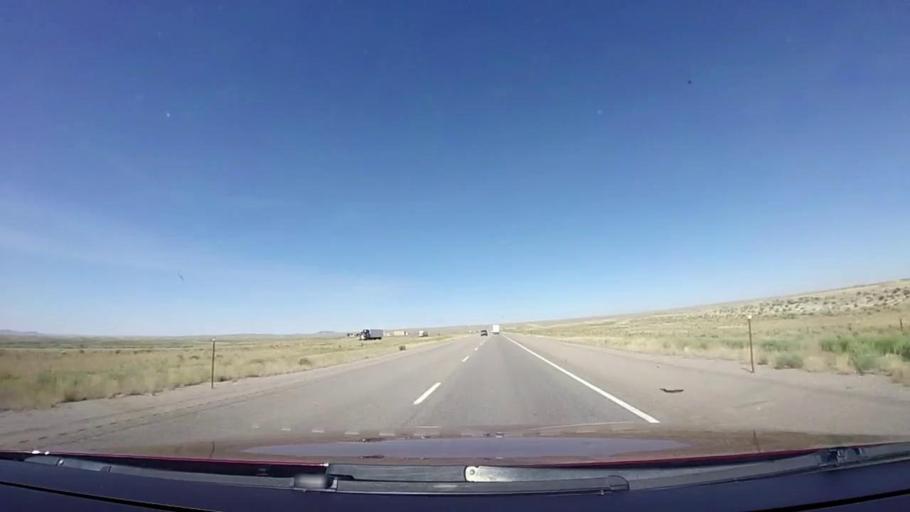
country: US
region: Wyoming
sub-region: Sweetwater County
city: Rock Springs
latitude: 41.6396
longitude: -108.4759
